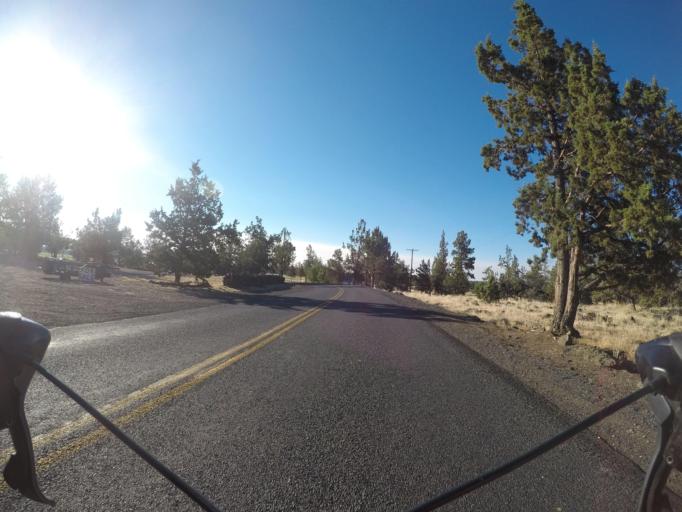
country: US
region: Oregon
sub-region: Deschutes County
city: Redmond
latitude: 44.2663
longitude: -121.2486
